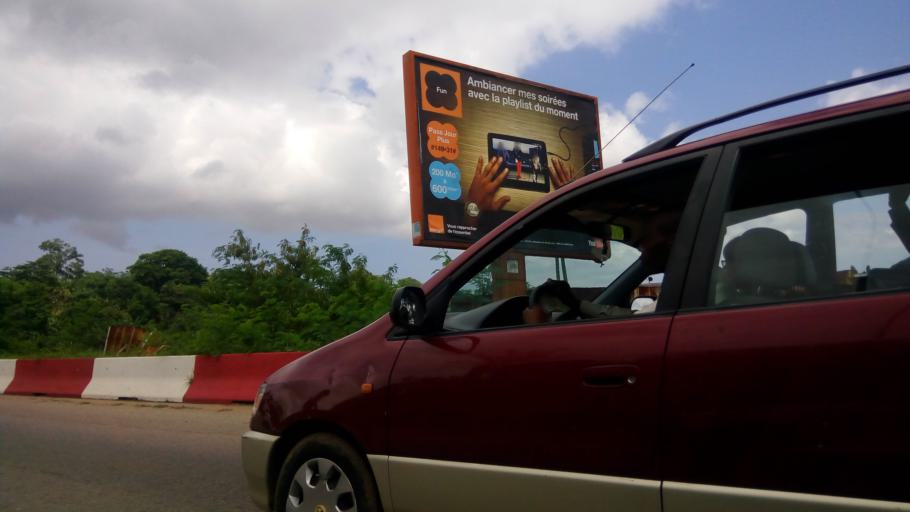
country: CI
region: Lagunes
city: Abidjan
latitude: 5.3346
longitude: -4.0136
